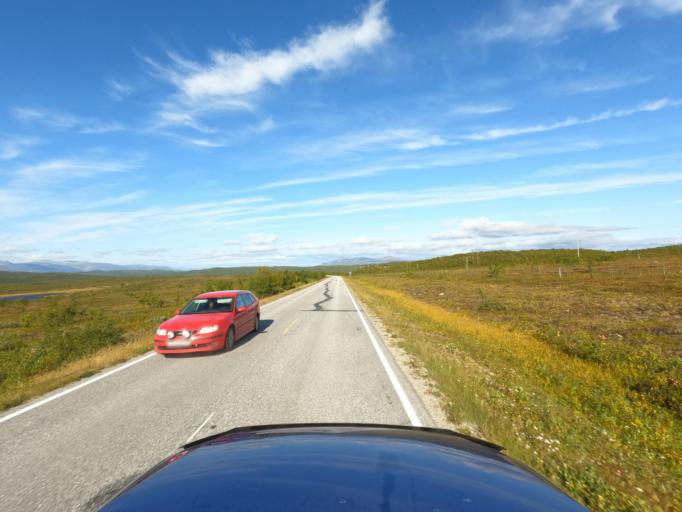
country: NO
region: Finnmark Fylke
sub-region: Karasjok
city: Karasjohka
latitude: 69.7305
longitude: 25.2343
